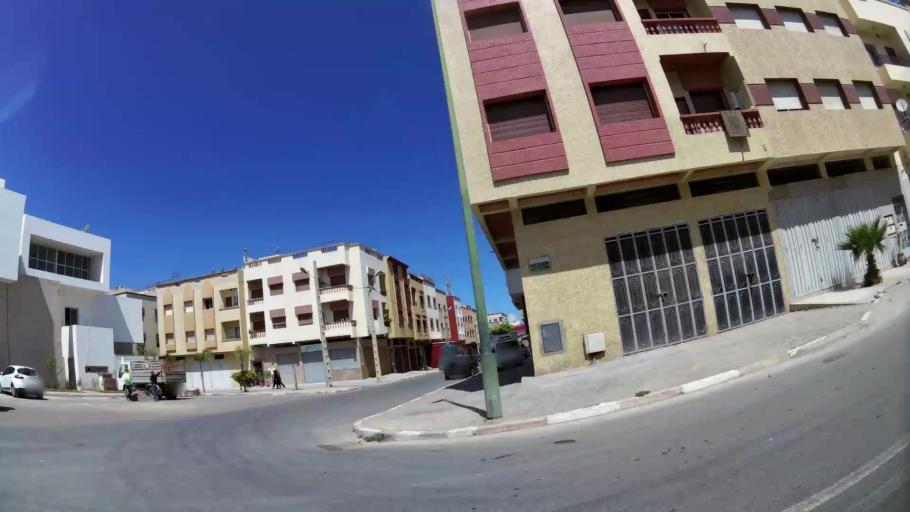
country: MA
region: Rabat-Sale-Zemmour-Zaer
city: Sale
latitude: 34.0728
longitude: -6.7916
